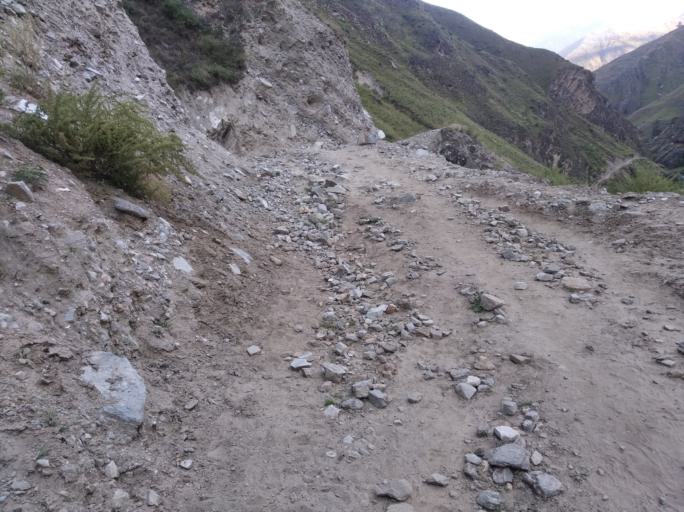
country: NP
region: Western Region
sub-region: Dhawalagiri Zone
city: Jomsom
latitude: 28.9181
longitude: 82.9701
